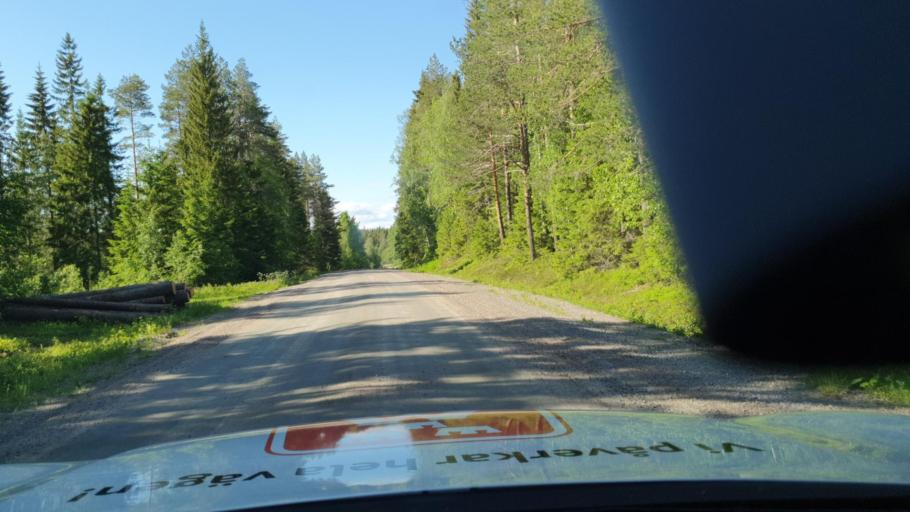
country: SE
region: Vaesterbotten
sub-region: Vannas Kommun
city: Vaennaes
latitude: 63.8390
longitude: 19.6296
